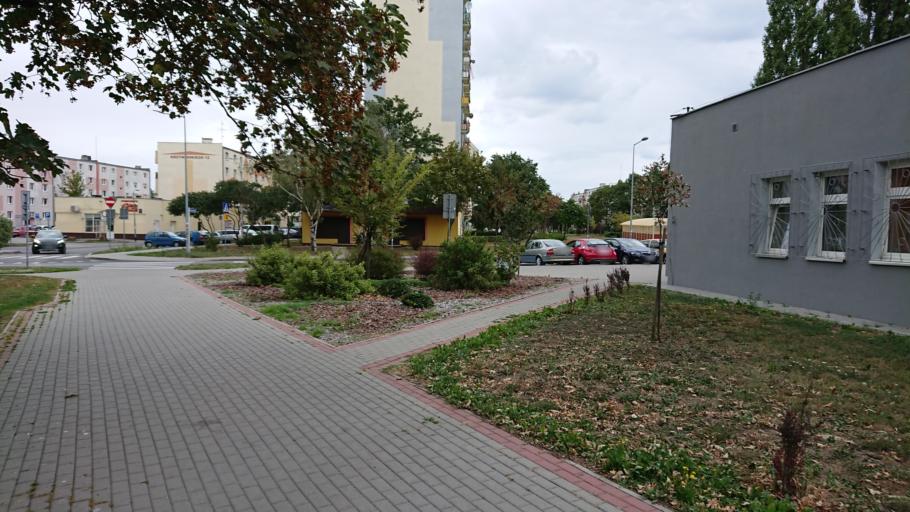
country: PL
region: Kujawsko-Pomorskie
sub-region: Powiat inowroclawski
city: Inowroclaw
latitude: 52.7866
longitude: 18.2503
